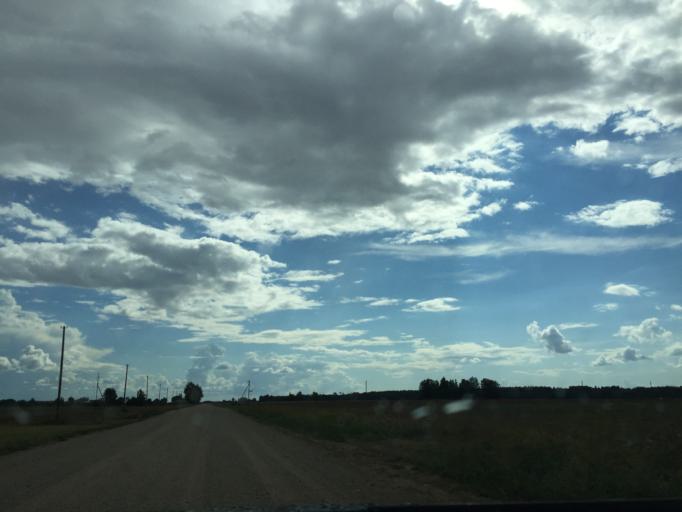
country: LT
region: Siauliu apskritis
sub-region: Joniskis
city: Joniskis
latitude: 56.3303
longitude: 23.5614
